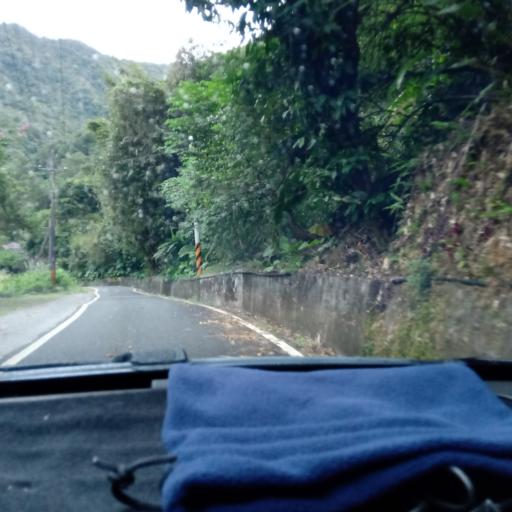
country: TW
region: Taiwan
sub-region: Yilan
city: Yilan
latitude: 24.8076
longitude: 121.7012
